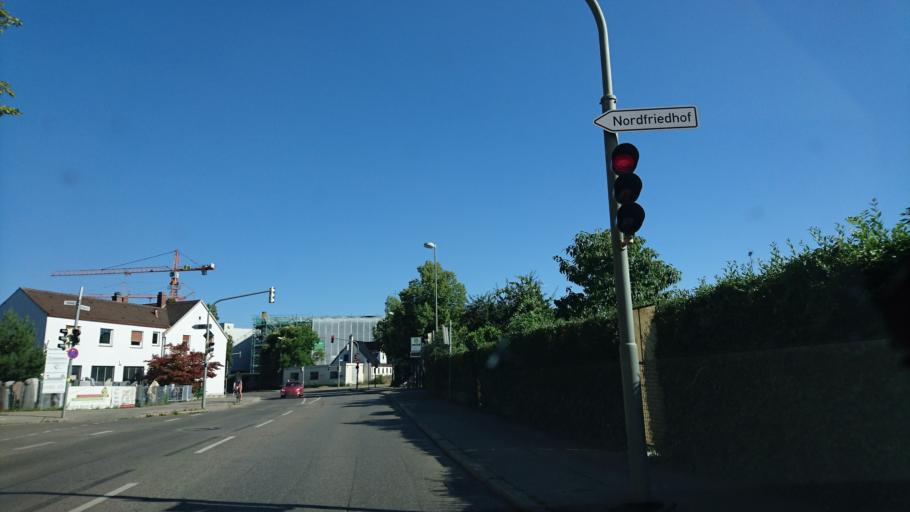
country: DE
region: Bavaria
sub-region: Swabia
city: Augsburg
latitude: 48.3886
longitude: 10.8735
